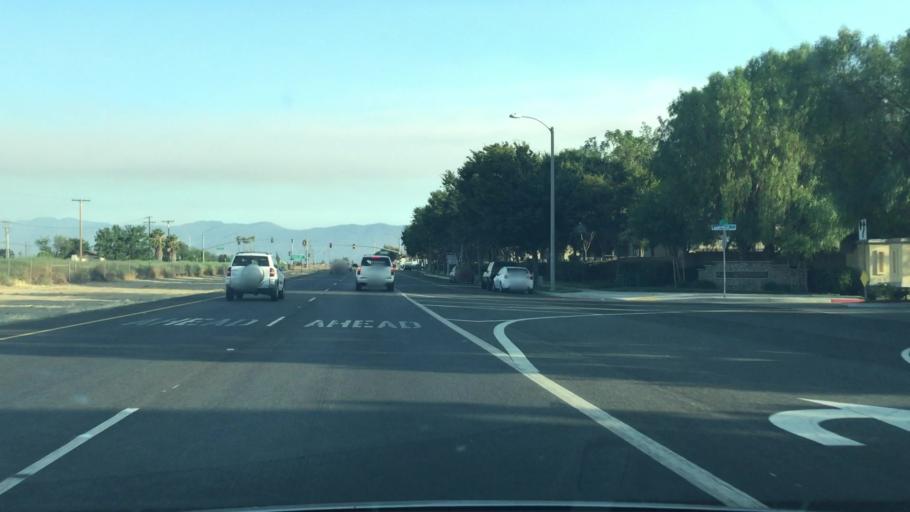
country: US
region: California
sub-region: San Bernardino County
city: Chino
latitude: 34.0142
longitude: -117.6509
